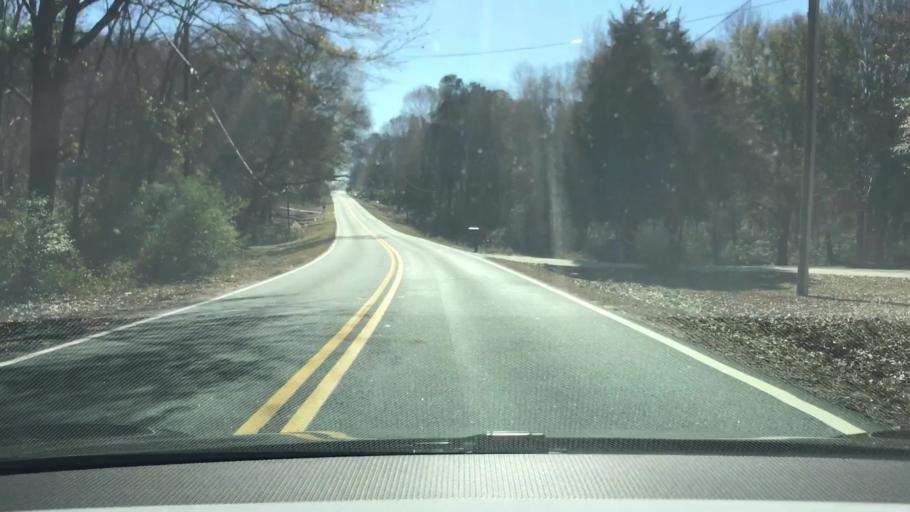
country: US
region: Georgia
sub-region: Walton County
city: Monroe
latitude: 33.8413
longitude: -83.7364
